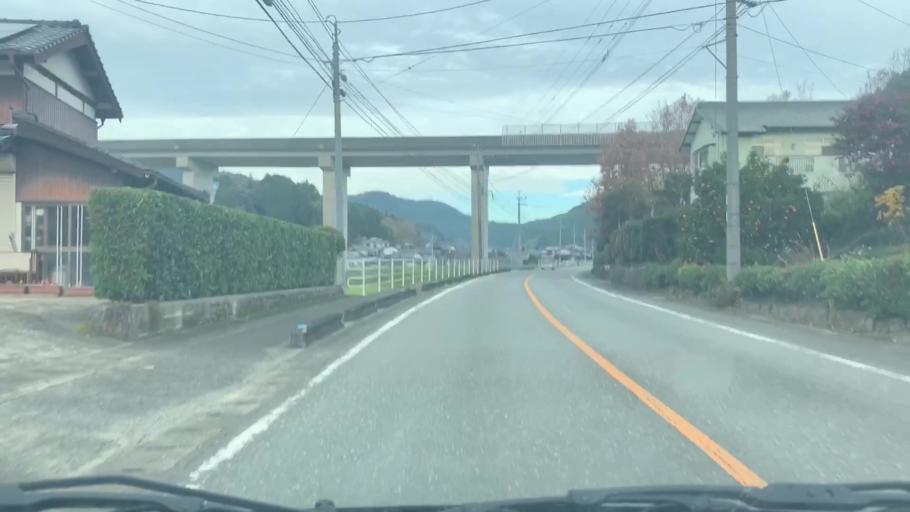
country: JP
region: Saga Prefecture
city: Ureshinomachi-shimojuku
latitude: 33.1424
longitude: 129.9768
